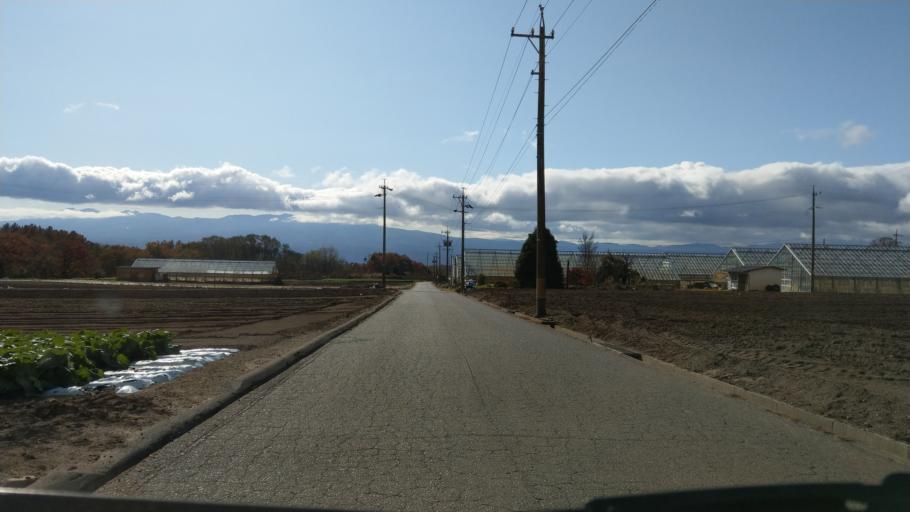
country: JP
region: Nagano
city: Komoro
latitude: 36.3179
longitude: 138.4833
